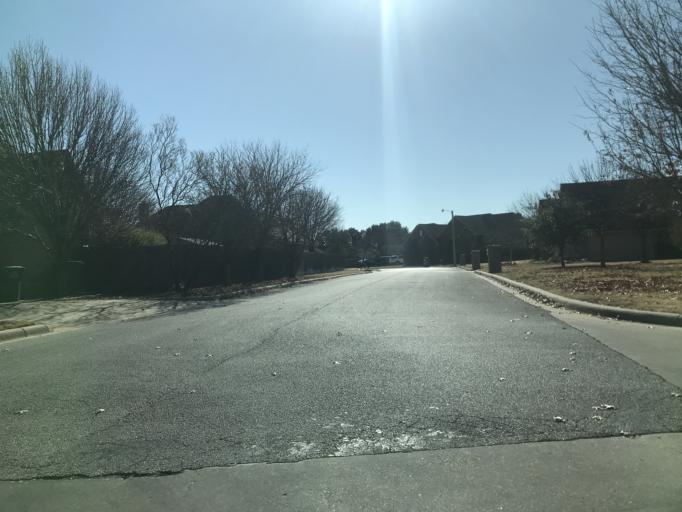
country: US
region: Texas
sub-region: Taylor County
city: Abilene
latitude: 32.3819
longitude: -99.7660
